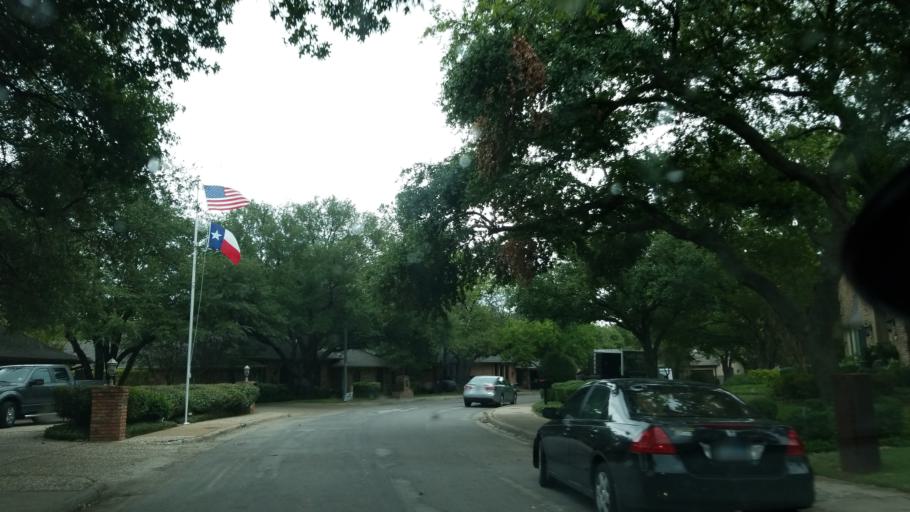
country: US
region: Texas
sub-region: Dallas County
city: Richardson
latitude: 32.8996
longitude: -96.7371
